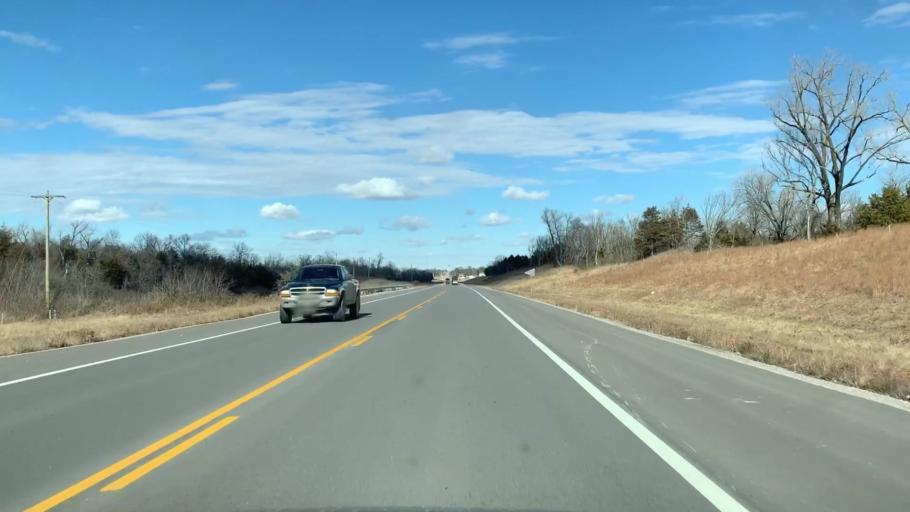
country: US
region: Kansas
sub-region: Crawford County
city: Pittsburg
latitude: 37.3274
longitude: -94.8322
